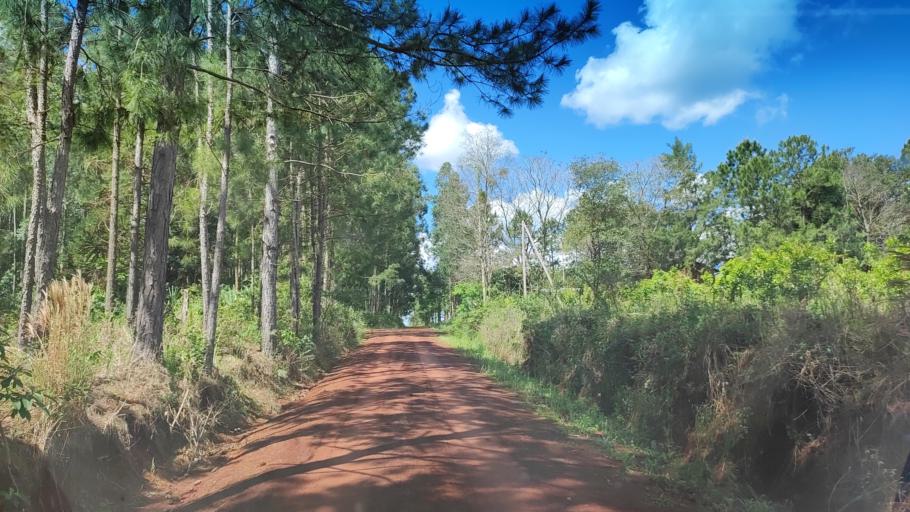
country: AR
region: Misiones
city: Ruiz de Montoya
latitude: -26.9528
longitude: -55.0240
